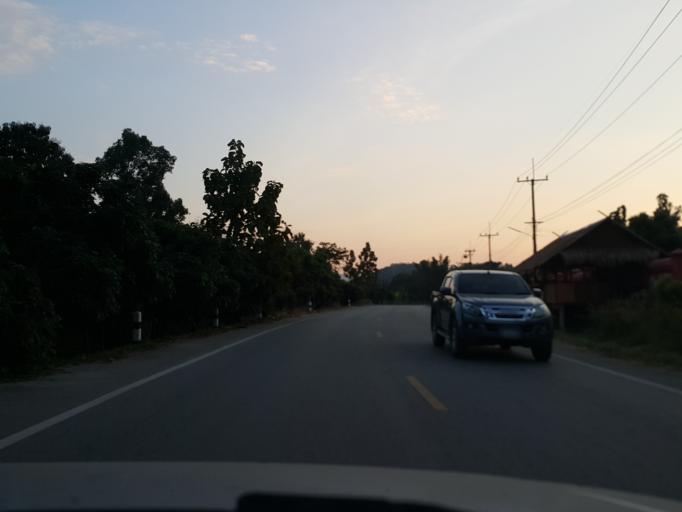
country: TH
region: Lamphun
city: Ban Thi
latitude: 18.5760
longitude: 99.2593
